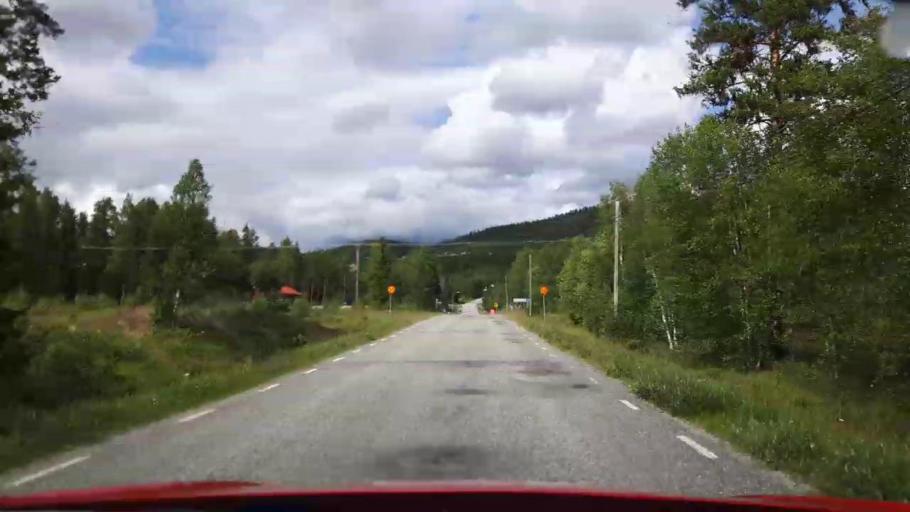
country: NO
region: Hedmark
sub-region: Engerdal
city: Engerdal
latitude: 62.4329
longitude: 12.6794
